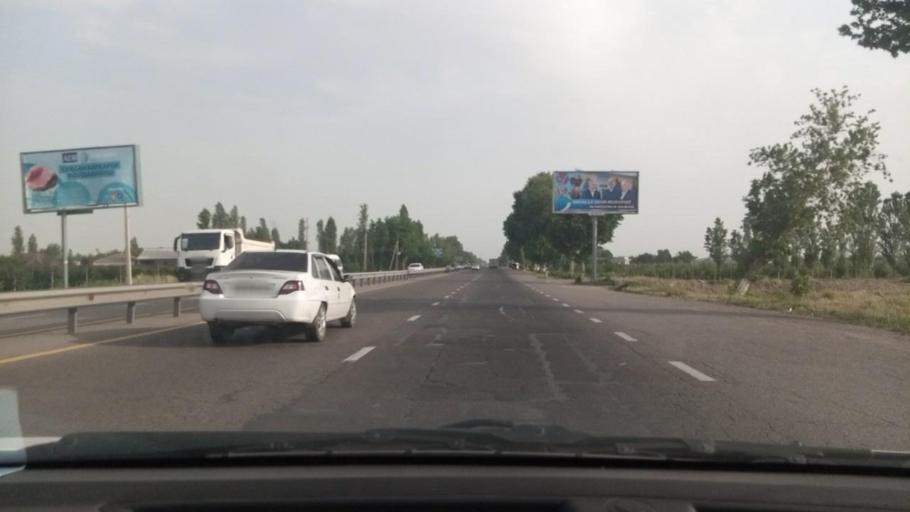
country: UZ
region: Toshkent Shahri
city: Bektemir
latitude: 41.2282
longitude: 69.4023
